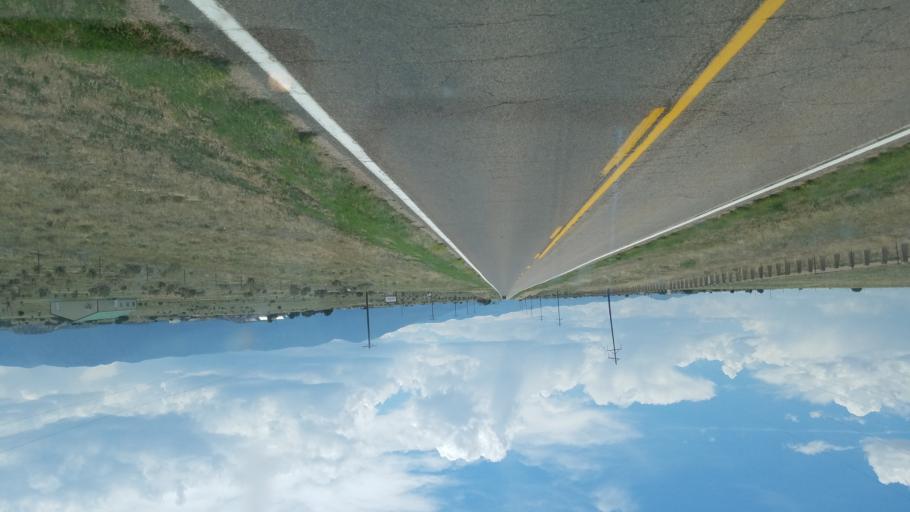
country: US
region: Colorado
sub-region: Fremont County
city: Florence
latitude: 38.3545
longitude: -105.1071
